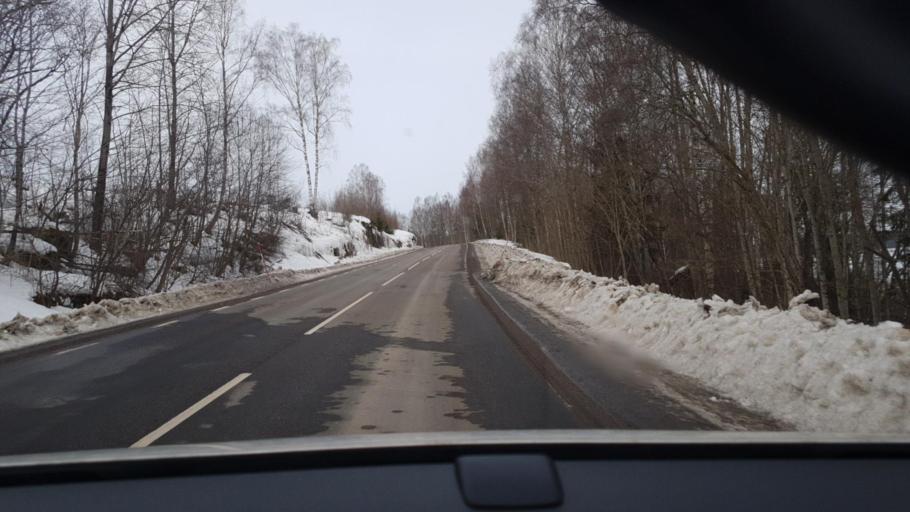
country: SE
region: Vaermland
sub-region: Eda Kommun
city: Amotfors
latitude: 59.7198
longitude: 12.4279
